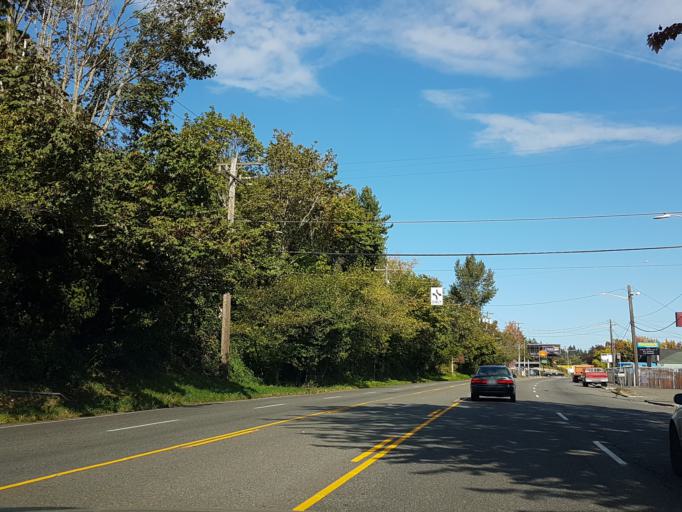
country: US
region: Washington
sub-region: King County
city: Lake Forest Park
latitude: 47.7064
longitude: -122.3016
